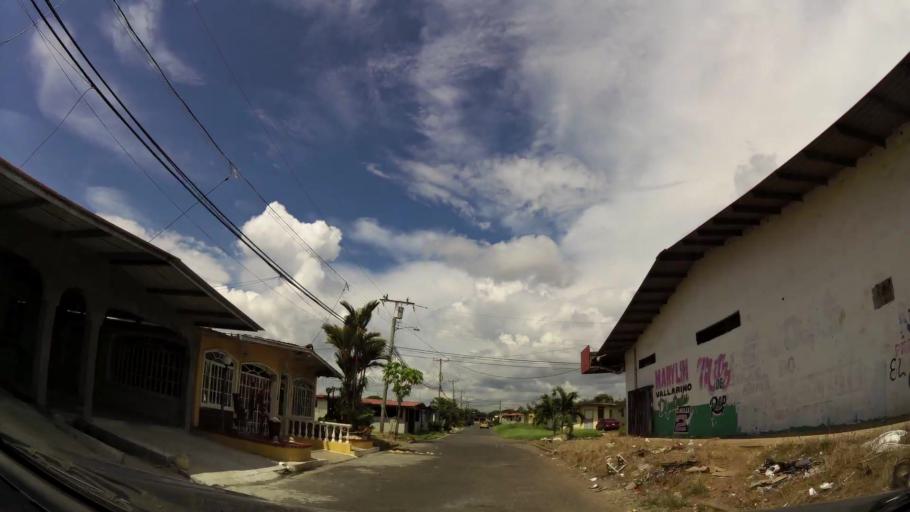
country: PA
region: Panama
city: Nuevo Arraijan
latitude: 8.9059
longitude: -79.7137
